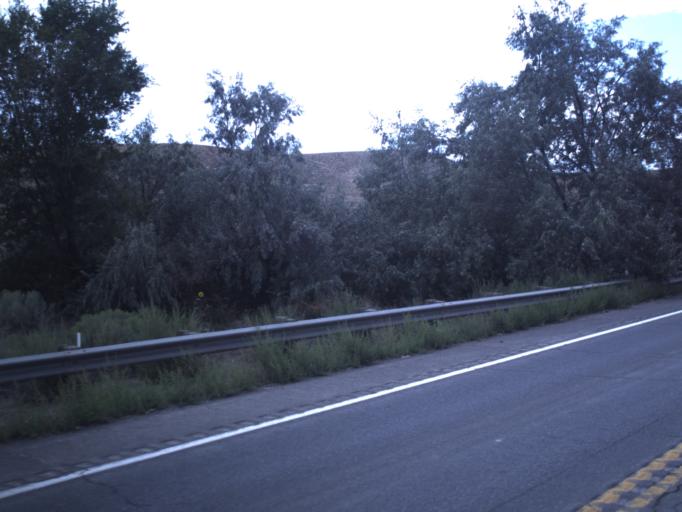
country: US
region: Utah
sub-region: Duchesne County
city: Duchesne
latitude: 40.1529
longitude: -110.2355
